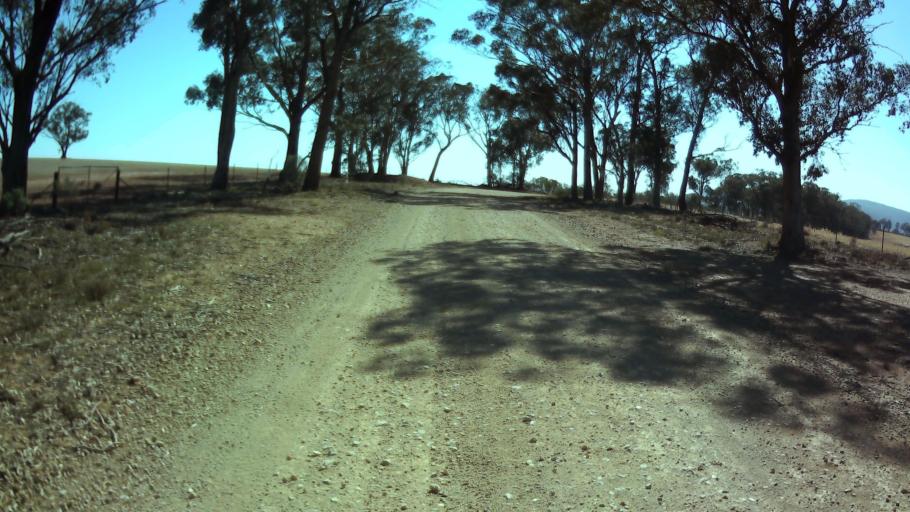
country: AU
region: New South Wales
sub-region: Weddin
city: Grenfell
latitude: -33.9020
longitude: 147.8662
